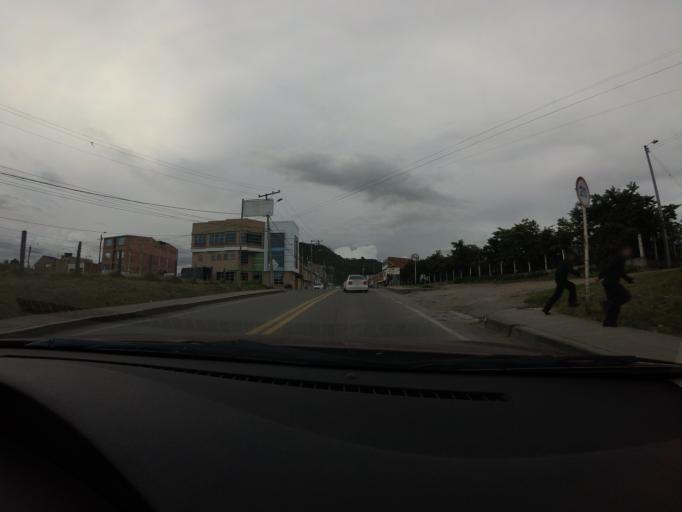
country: CO
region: Cundinamarca
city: Sopo
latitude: 4.9403
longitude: -73.9604
